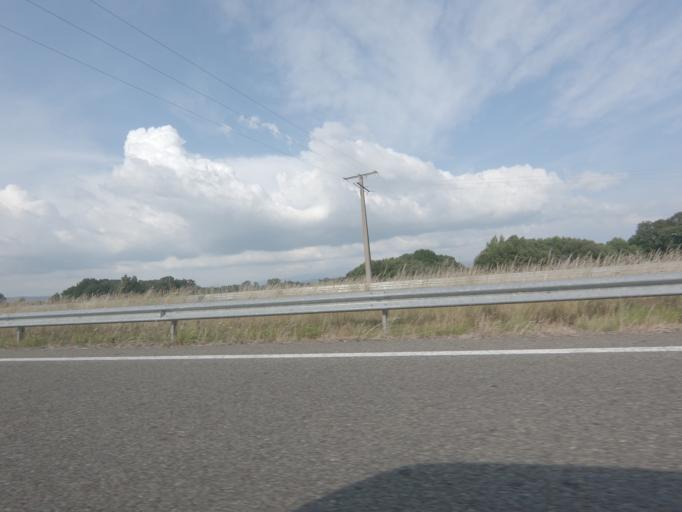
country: ES
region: Galicia
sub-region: Provincia de Ourense
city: Xinzo de Limia
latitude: 42.1259
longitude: -7.7403
